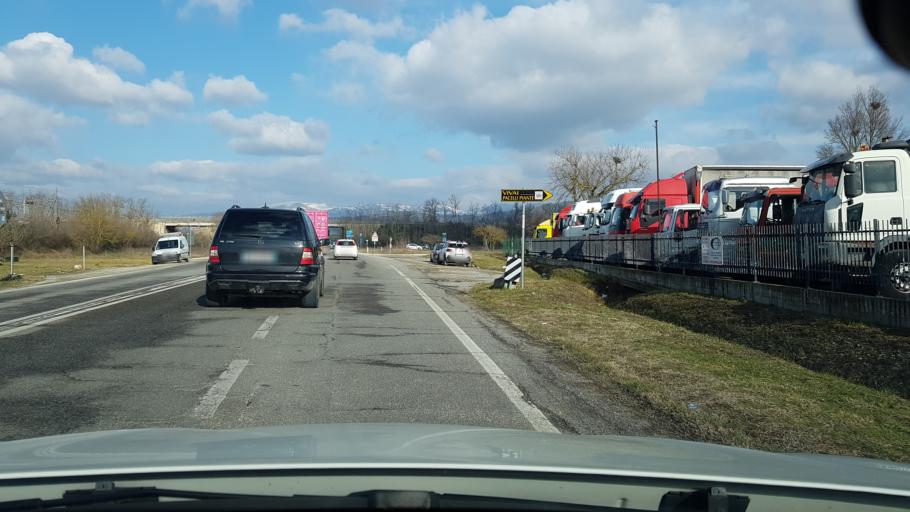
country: IT
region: Tuscany
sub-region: Province of Arezzo
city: Terontola
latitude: 43.1876
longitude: 12.0134
